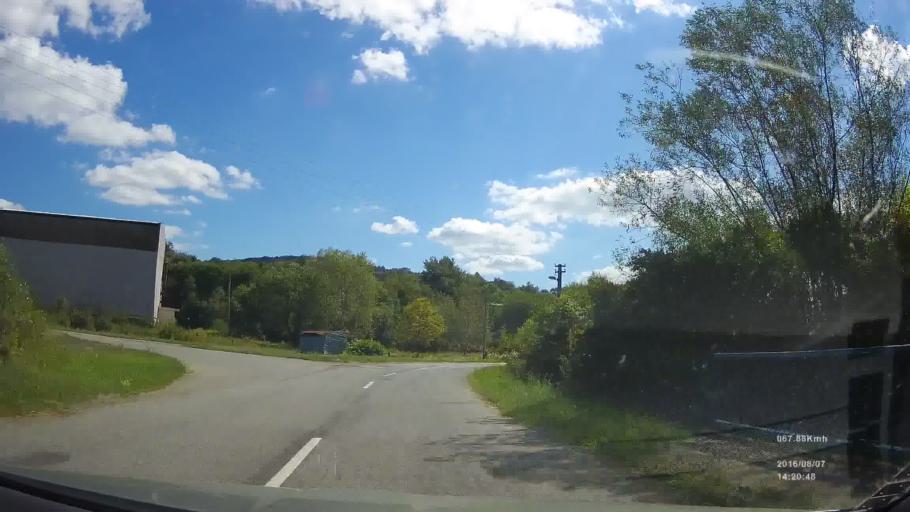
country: SK
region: Presovsky
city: Stropkov
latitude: 49.2858
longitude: 21.7610
